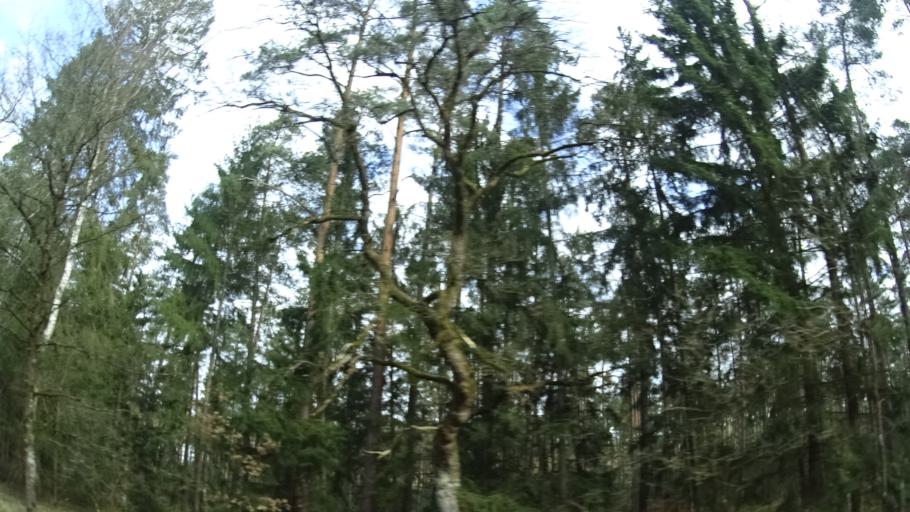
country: DE
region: Bavaria
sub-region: Regierungsbezirk Mittelfranken
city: Winkelhaid
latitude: 49.4077
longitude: 11.3035
